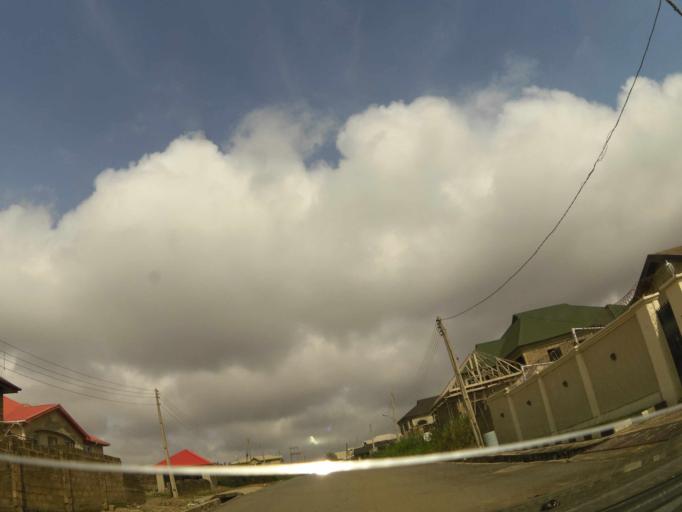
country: NG
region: Oyo
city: Ibadan
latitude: 7.4359
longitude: 3.9601
